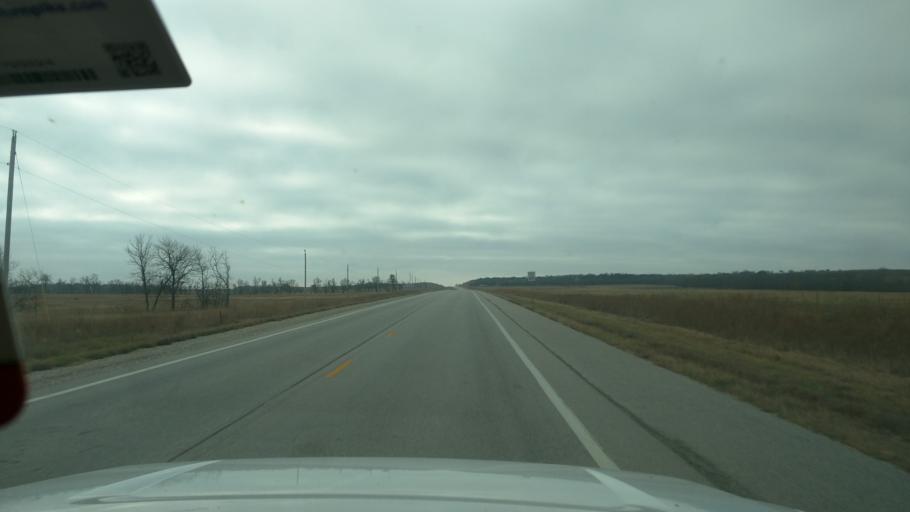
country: US
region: Kansas
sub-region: Elk County
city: Howard
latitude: 37.6183
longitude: -96.2532
